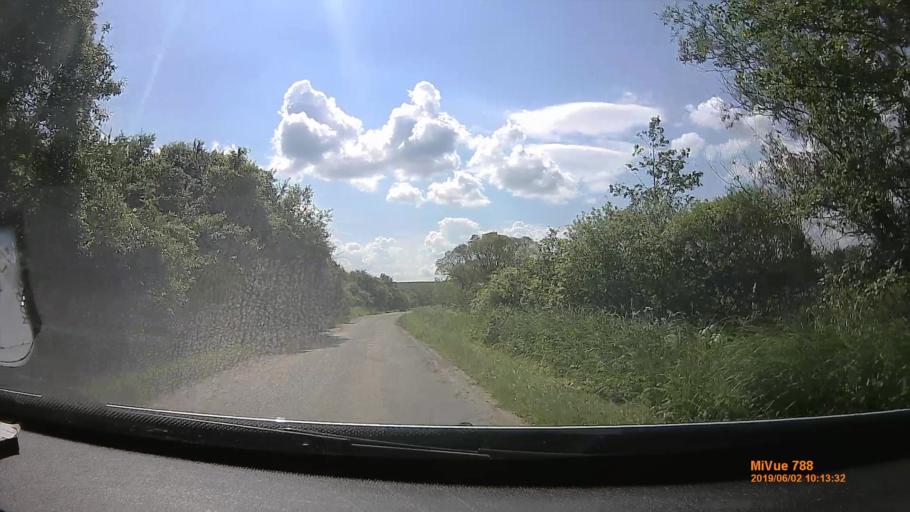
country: HU
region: Borsod-Abauj-Zemplen
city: Szendro
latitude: 48.5144
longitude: 20.7857
